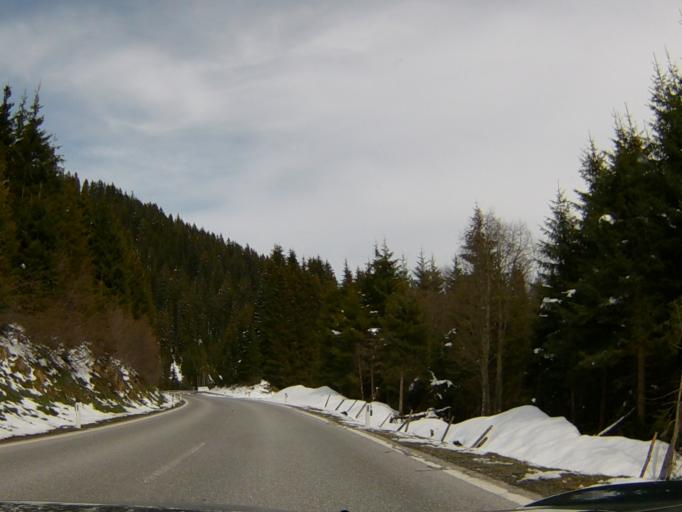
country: AT
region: Salzburg
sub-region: Politischer Bezirk Zell am See
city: Krimml
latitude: 47.2428
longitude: 12.0953
